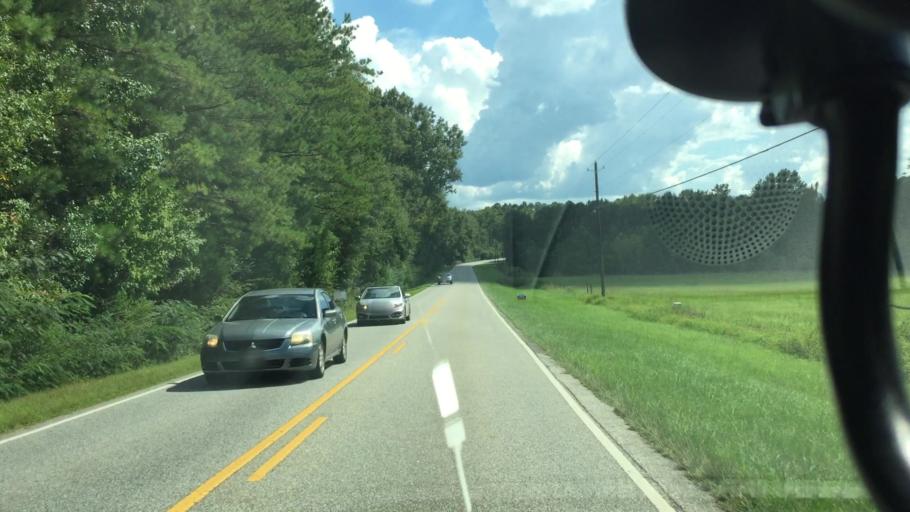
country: US
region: Alabama
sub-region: Lee County
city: Auburn
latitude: 32.5661
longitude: -85.5242
